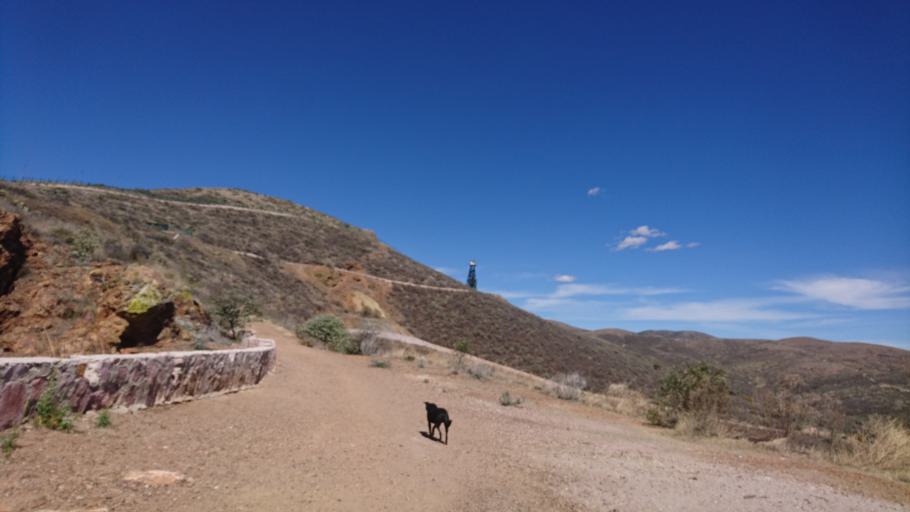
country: MX
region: Zacatecas
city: Zacatecas
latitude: 22.7774
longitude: -102.5476
